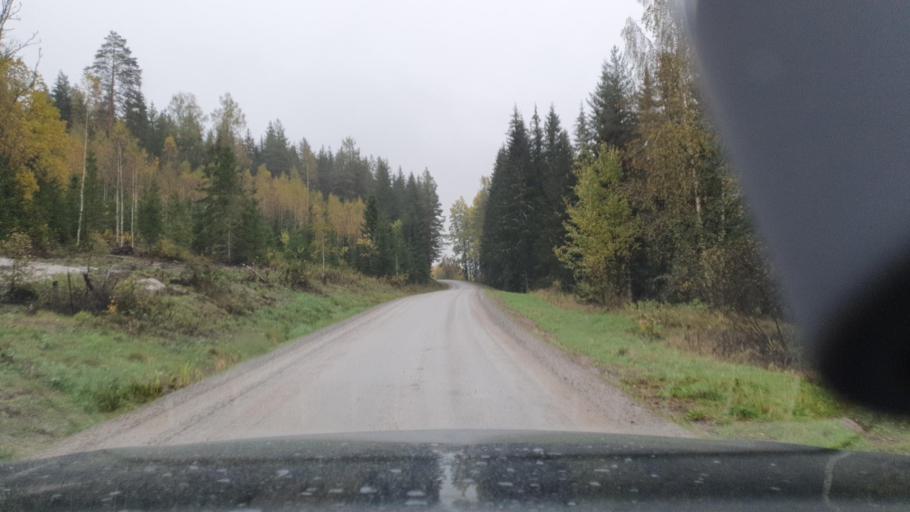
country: SE
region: Vaermland
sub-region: Arvika Kommun
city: Arvika
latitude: 59.6137
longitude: 12.9032
